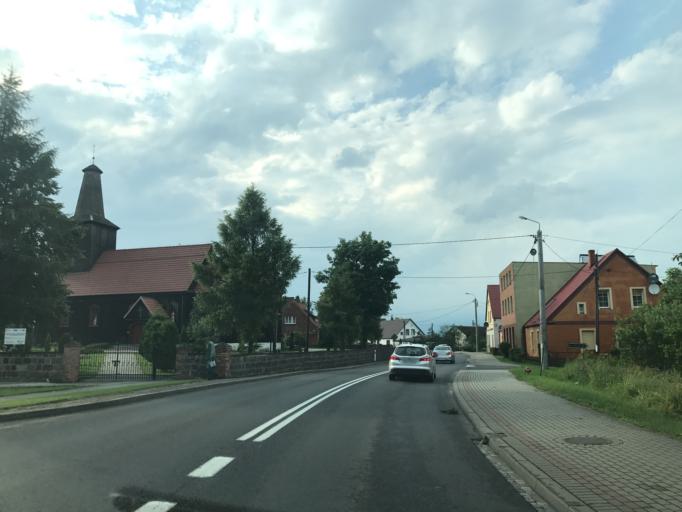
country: PL
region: Pomeranian Voivodeship
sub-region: Powiat czluchowski
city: Przechlewo
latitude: 53.7364
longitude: 17.1928
